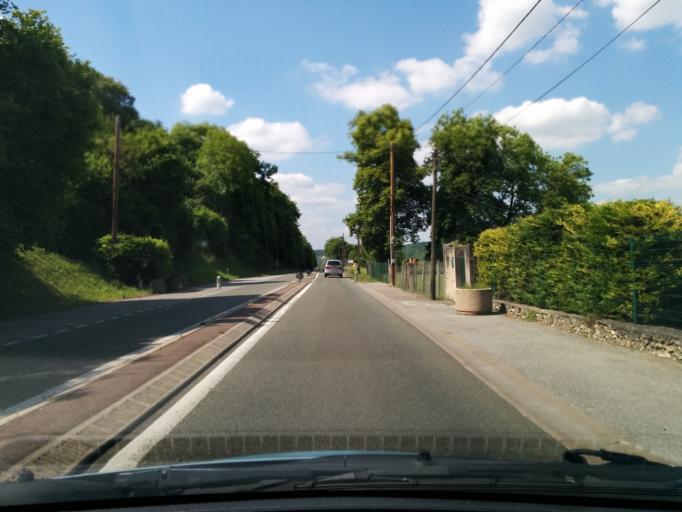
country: FR
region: Ile-de-France
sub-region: Departement des Yvelines
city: Limetz-Villez
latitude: 49.0626
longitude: 1.5225
